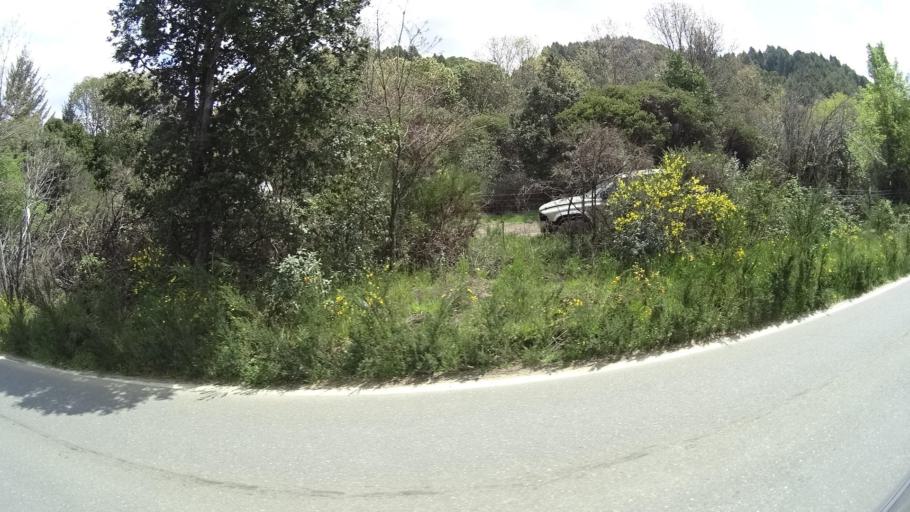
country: US
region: California
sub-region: Humboldt County
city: Redway
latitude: 40.0596
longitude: -123.9688
